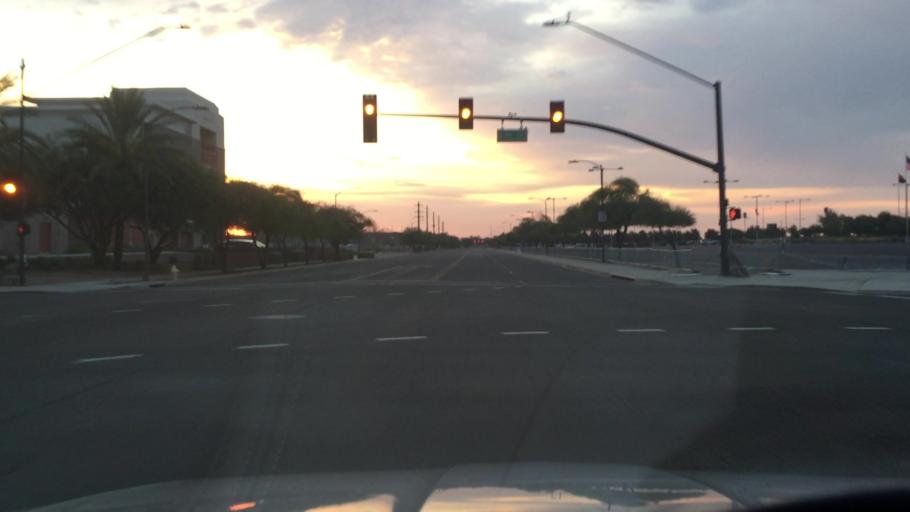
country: US
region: Arizona
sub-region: Maricopa County
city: Peoria
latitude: 33.5301
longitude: -112.2649
